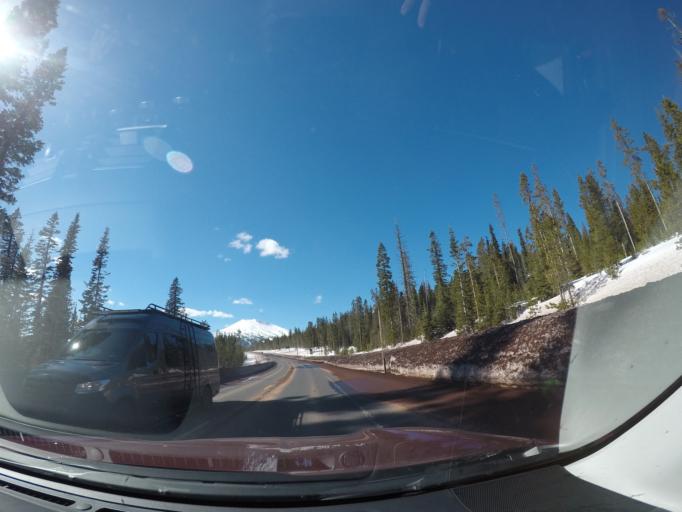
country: US
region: Oregon
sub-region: Deschutes County
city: Sunriver
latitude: 43.9839
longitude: -121.6018
